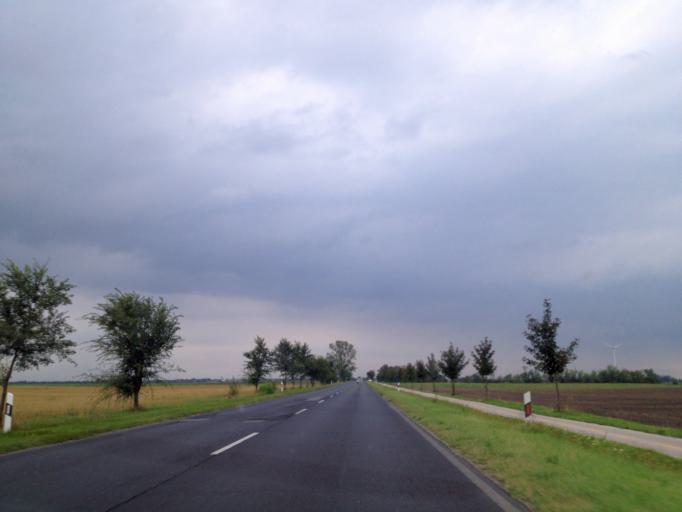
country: HU
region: Gyor-Moson-Sopron
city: Mosonmagyarovar
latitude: 47.8872
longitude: 17.2349
